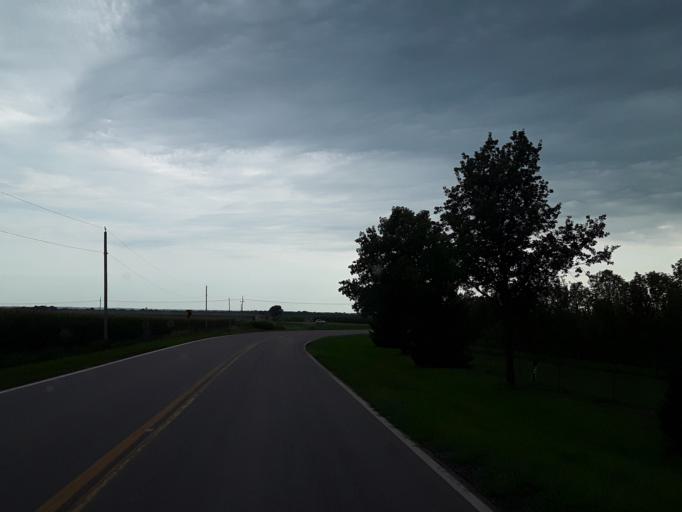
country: US
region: Nebraska
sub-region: Saunders County
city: Yutan
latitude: 41.1935
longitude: -96.3968
